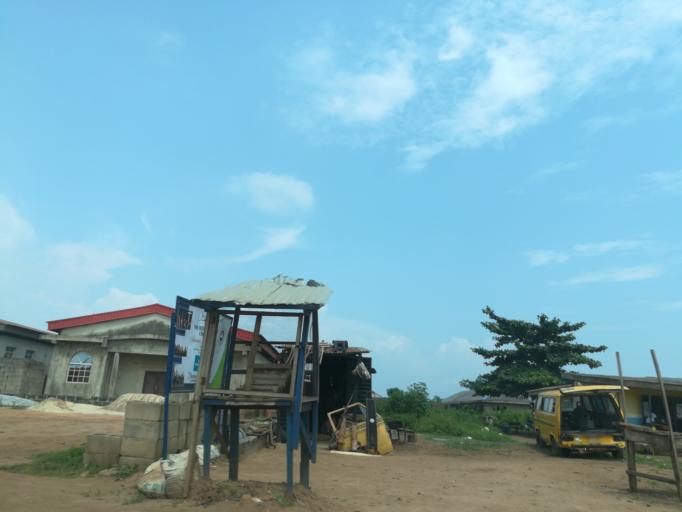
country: NG
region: Lagos
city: Ikorodu
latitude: 6.5927
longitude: 3.6246
